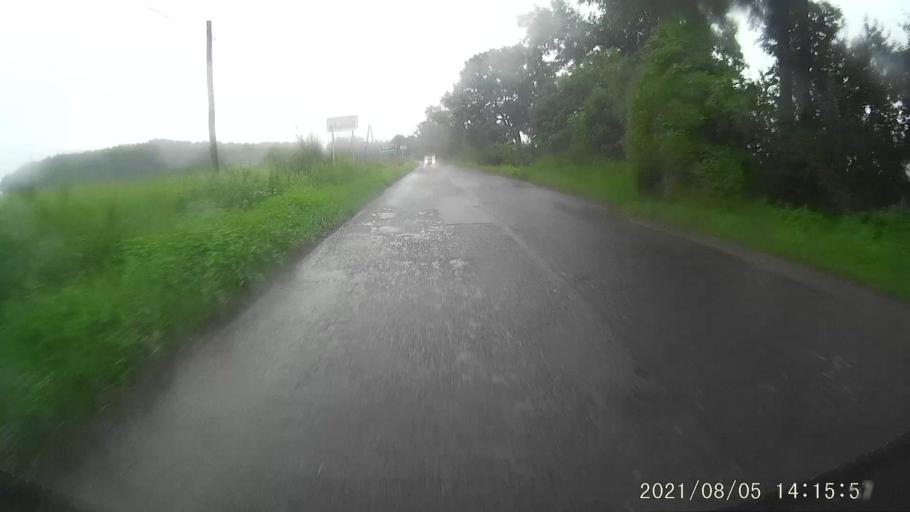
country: PL
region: Opole Voivodeship
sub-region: Powiat prudnicki
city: Biala
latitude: 50.4595
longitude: 17.7285
